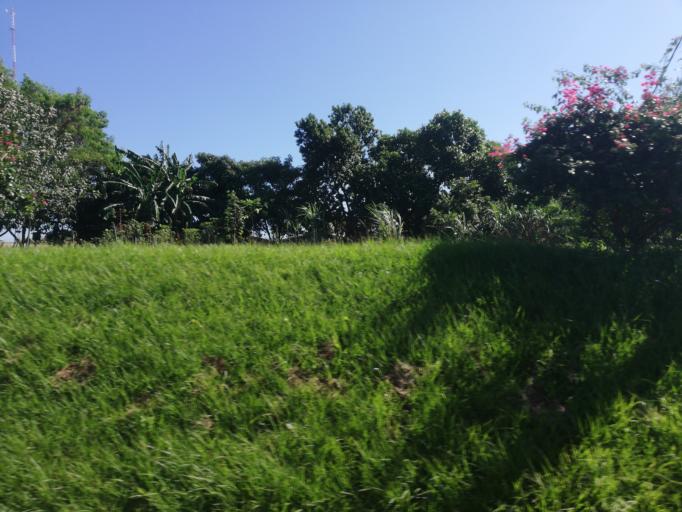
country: AR
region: Misiones
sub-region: Departamento de Iguazu
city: Puerto Iguazu
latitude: -25.5799
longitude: -54.5601
